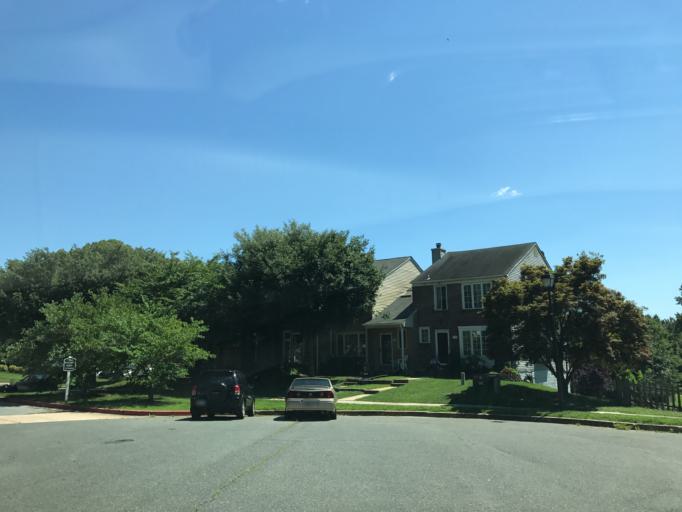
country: US
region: Maryland
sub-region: Baltimore County
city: Perry Hall
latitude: 39.3829
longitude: -76.4676
